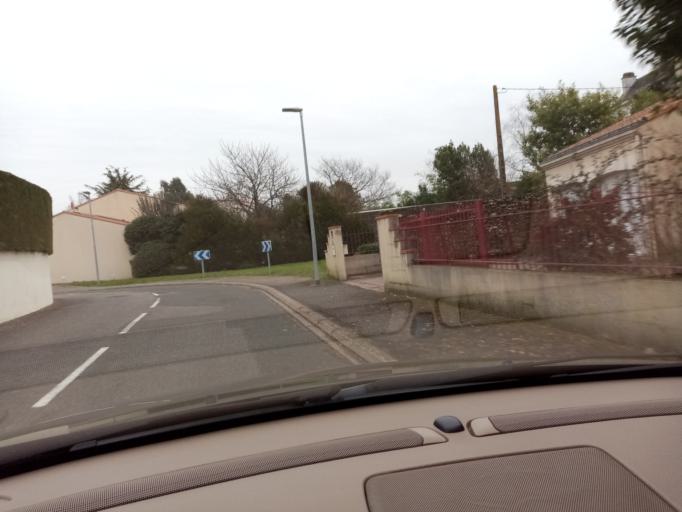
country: FR
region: Pays de la Loire
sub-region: Departement de la Loire-Atlantique
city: Saint-Sebastien-sur-Loire
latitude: 47.1997
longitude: -1.5133
